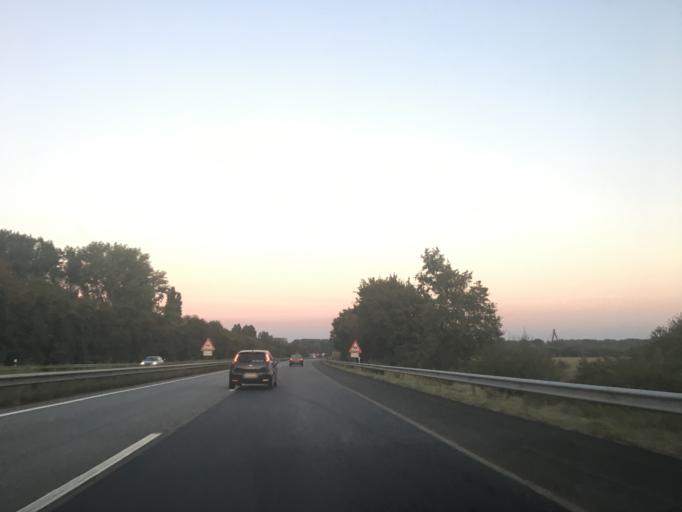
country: DE
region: Rheinland-Pfalz
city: Otterstadt
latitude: 49.3533
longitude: 8.4473
